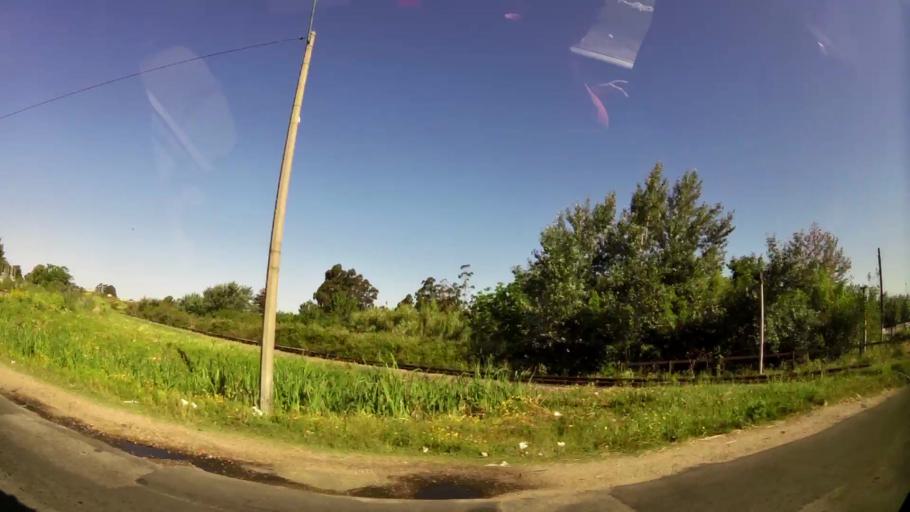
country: UY
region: Canelones
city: La Paz
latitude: -34.8152
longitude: -56.1710
